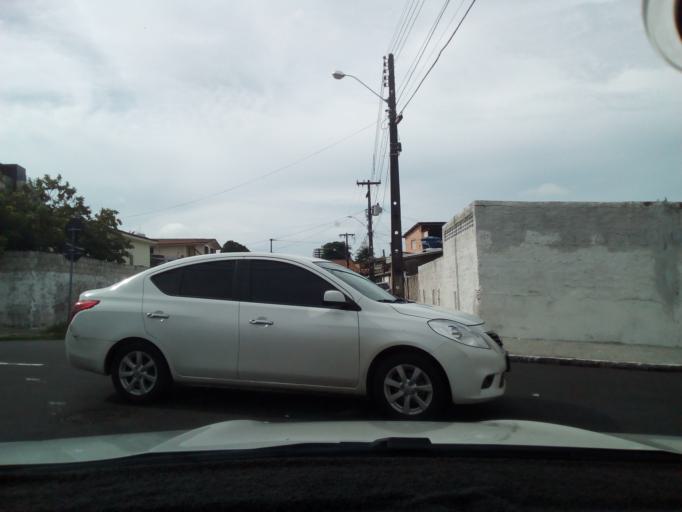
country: BR
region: Paraiba
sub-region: Joao Pessoa
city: Joao Pessoa
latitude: -7.1287
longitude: -34.8567
